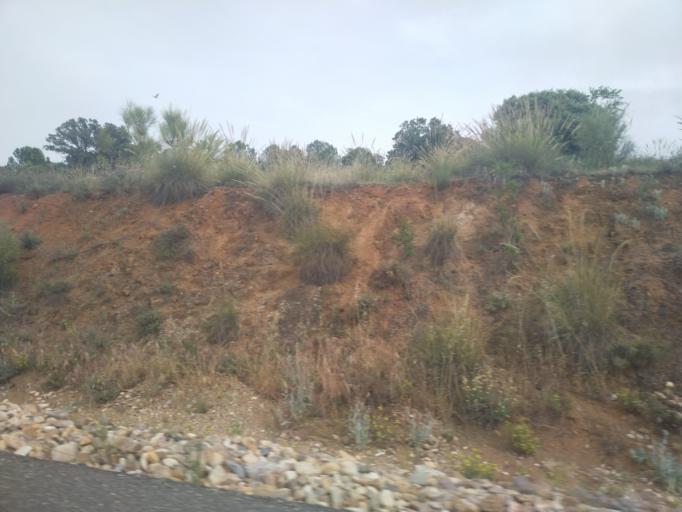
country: ES
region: Castille-La Mancha
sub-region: Province of Toledo
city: Guadamur
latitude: 39.8146
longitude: -4.1047
